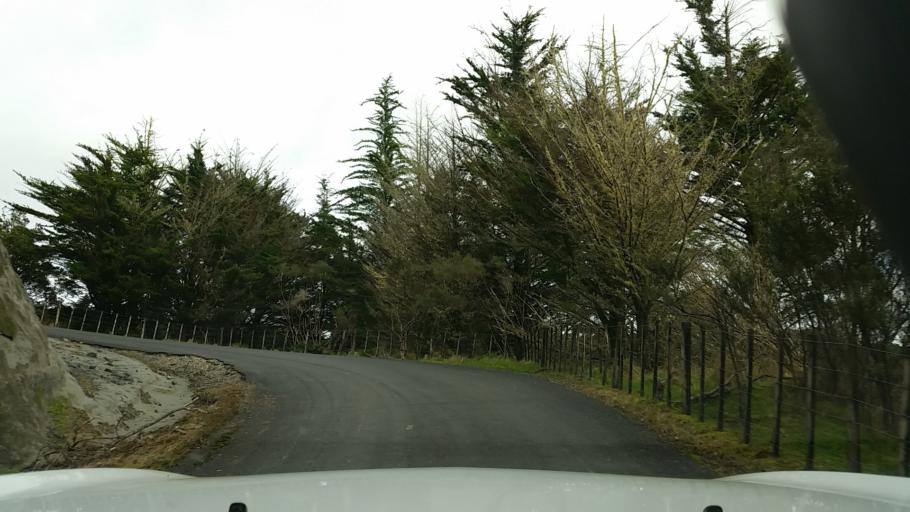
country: NZ
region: Taranaki
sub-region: New Plymouth District
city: Waitara
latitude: -38.9138
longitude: 174.7639
